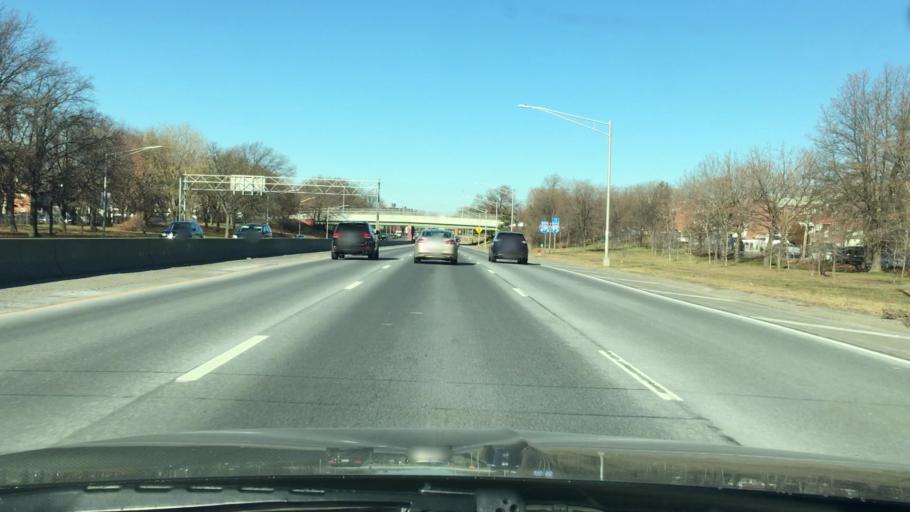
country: US
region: New York
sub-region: Bronx
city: The Bronx
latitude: 40.8300
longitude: -73.8193
